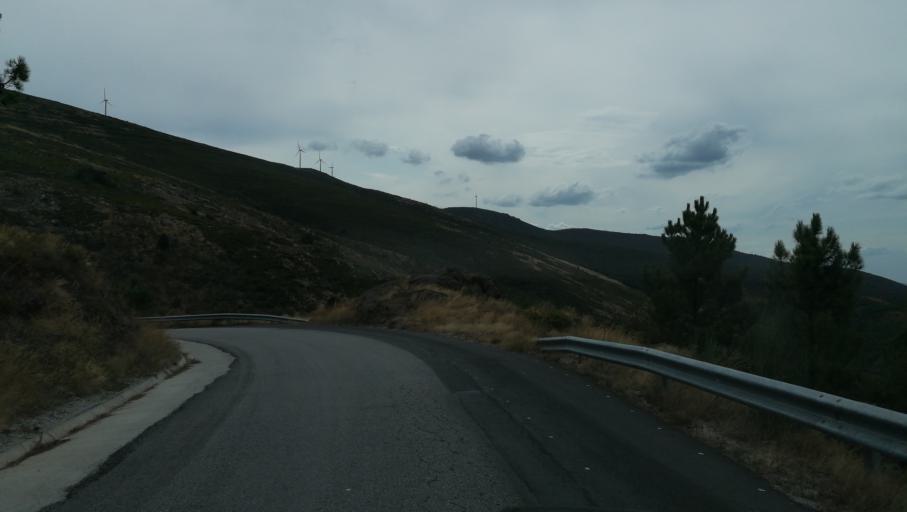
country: PT
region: Vila Real
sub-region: Vila Pouca de Aguiar
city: Vila Pouca de Aguiar
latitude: 41.5583
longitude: -7.7015
